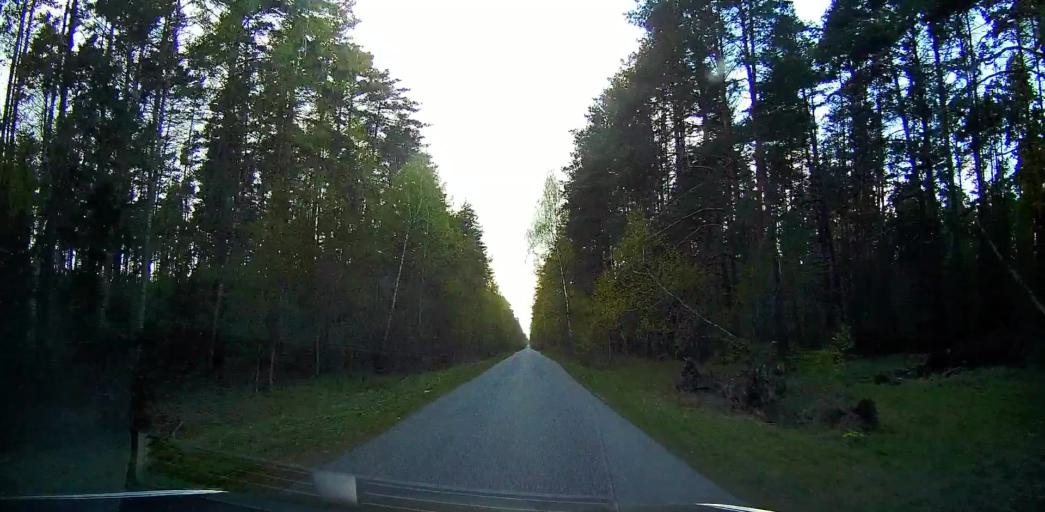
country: RU
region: Moskovskaya
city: Malyshevo
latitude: 55.5459
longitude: 38.3736
